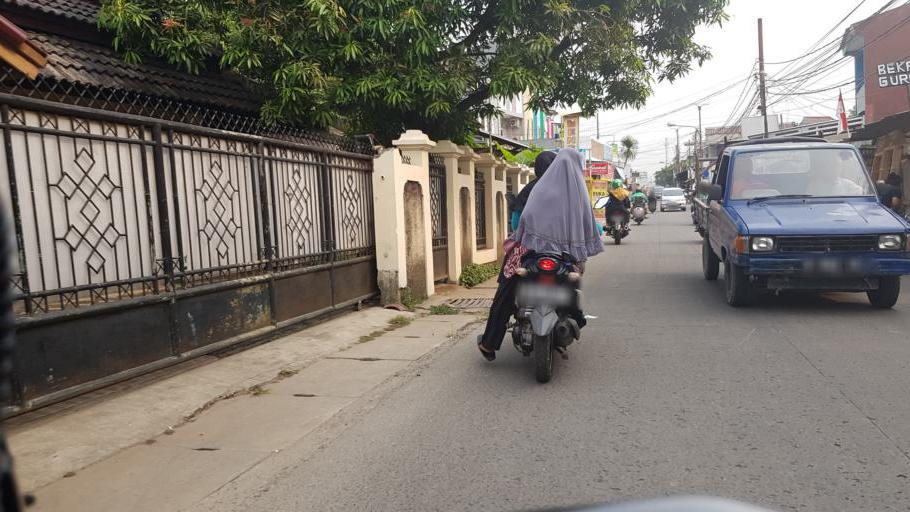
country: ID
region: West Java
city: Depok
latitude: -6.3594
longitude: 106.8431
